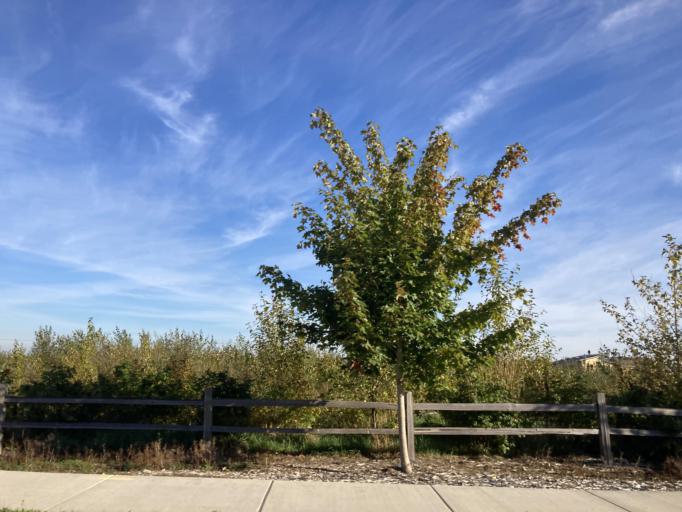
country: US
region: Washington
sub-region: Whatcom County
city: Marietta-Alderwood
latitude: 48.8151
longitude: -122.5029
